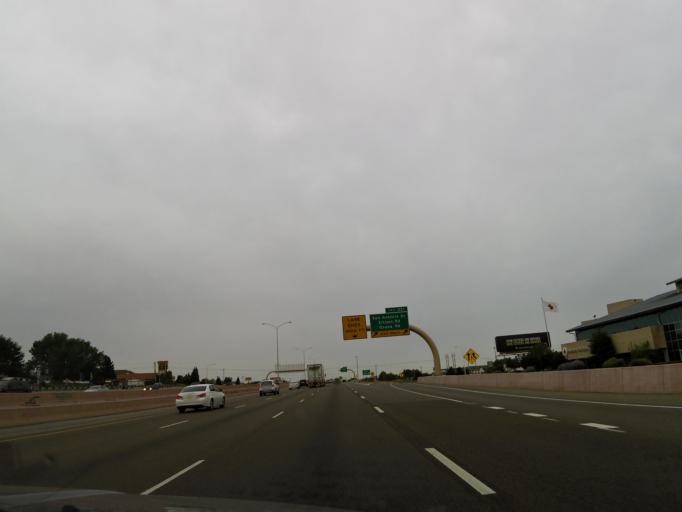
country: US
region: New Mexico
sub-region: Bernalillo County
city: North Valley
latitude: 35.1635
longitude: -106.5865
